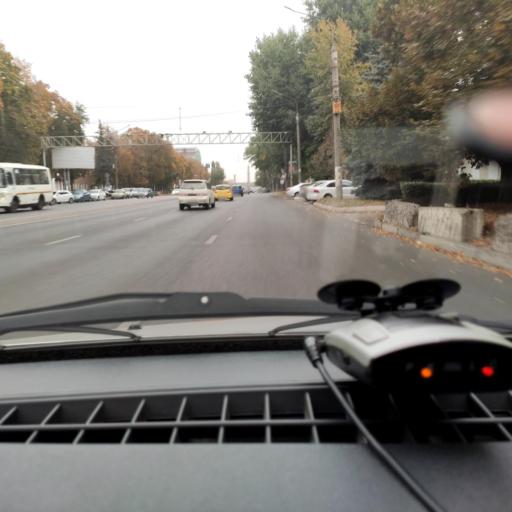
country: RU
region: Voronezj
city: Voronezh
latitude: 51.6767
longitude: 39.1713
